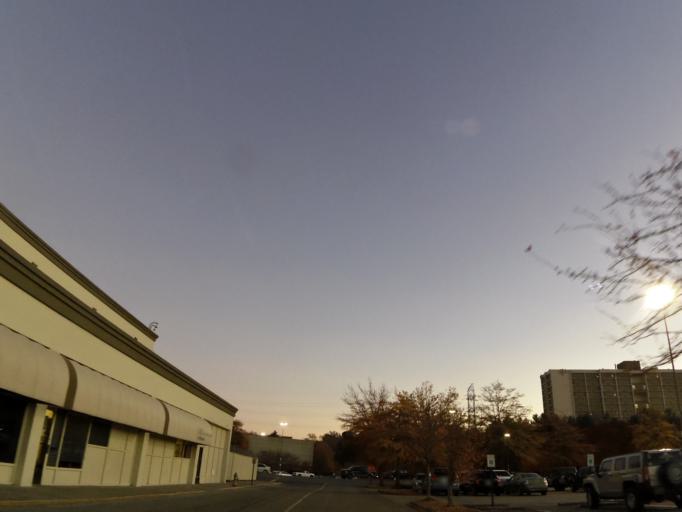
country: US
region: Tennessee
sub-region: Blount County
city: Louisville
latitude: 35.9244
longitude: -84.0393
